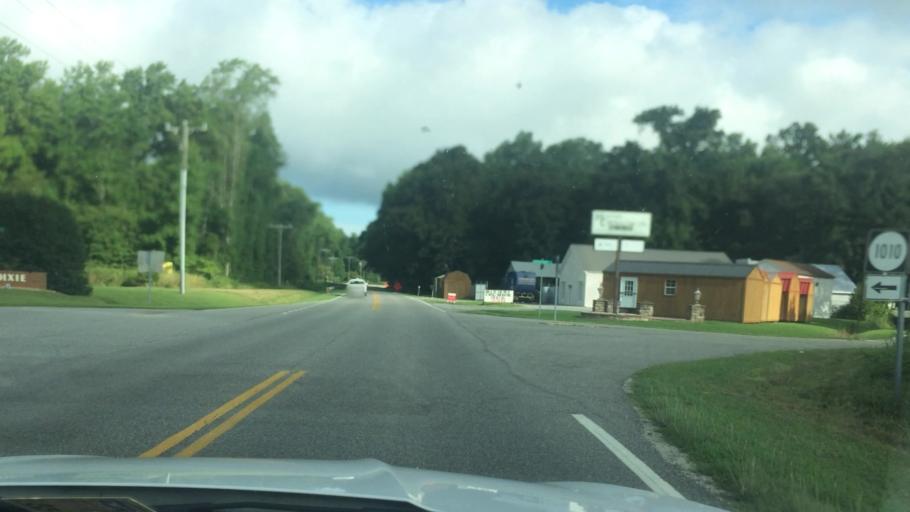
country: US
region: Virginia
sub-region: Middlesex County
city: Deltaville
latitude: 37.5024
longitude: -76.4158
